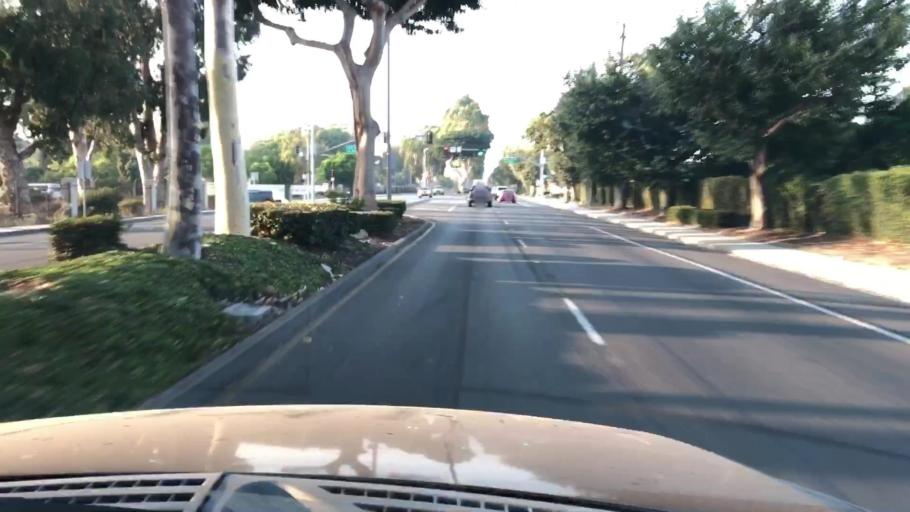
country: US
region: California
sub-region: Ventura County
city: Port Hueneme
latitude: 34.1602
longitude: -119.1951
